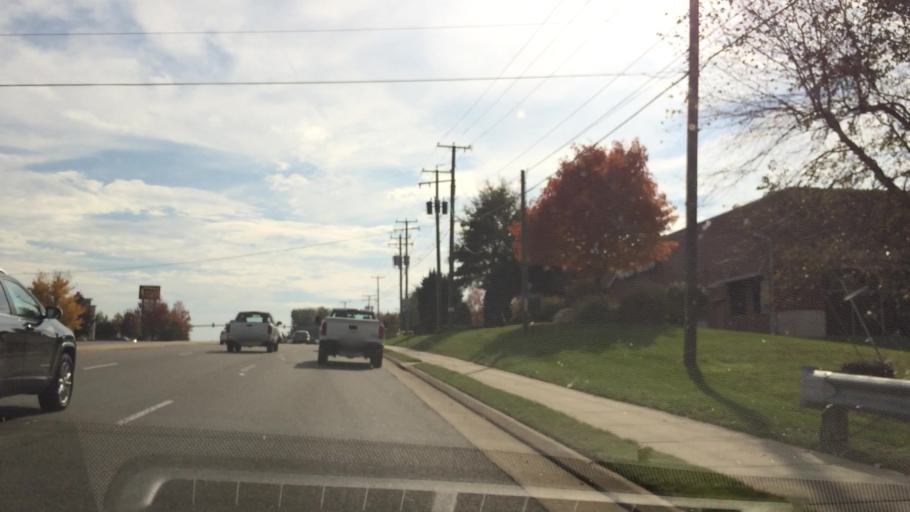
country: US
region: Virginia
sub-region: Henrico County
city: Glen Allen
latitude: 37.6709
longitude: -77.4611
